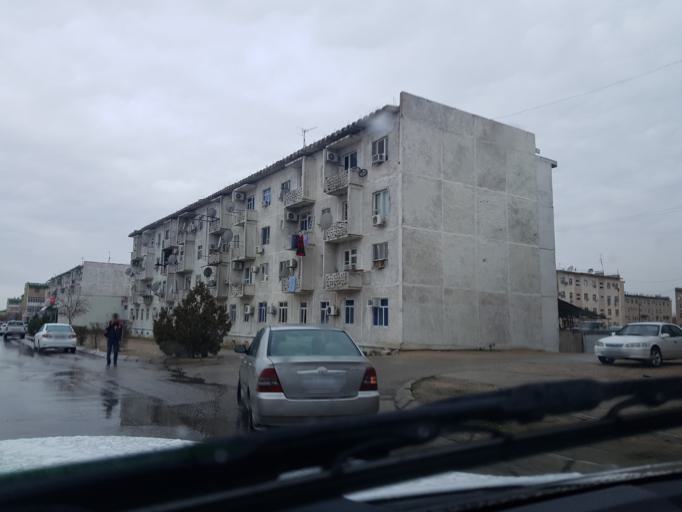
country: TM
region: Balkan
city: Balkanabat
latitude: 39.5253
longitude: 54.3587
